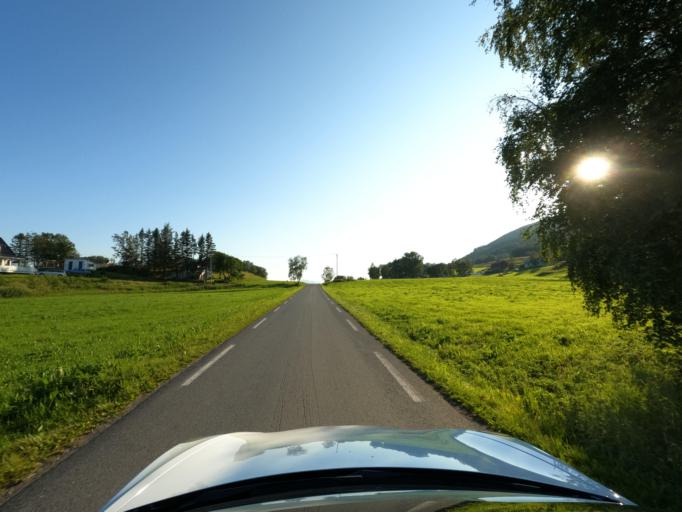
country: NO
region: Nordland
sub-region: Evenes
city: Randa
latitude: 68.4721
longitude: 16.8727
